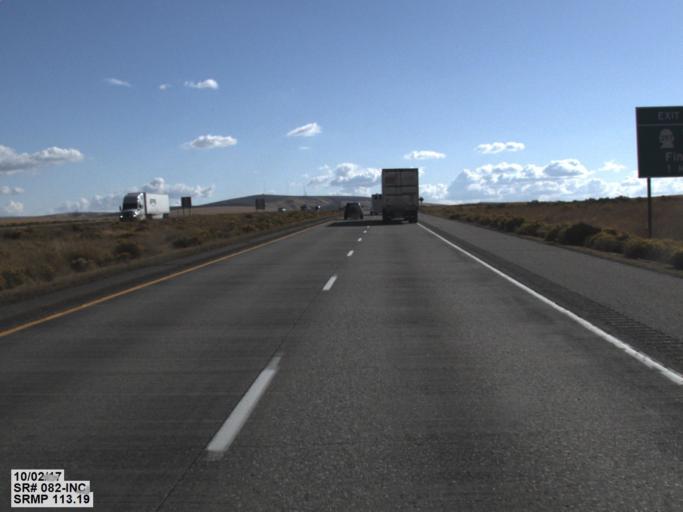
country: US
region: Washington
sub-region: Benton County
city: Kennewick
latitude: 46.1598
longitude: -119.2020
